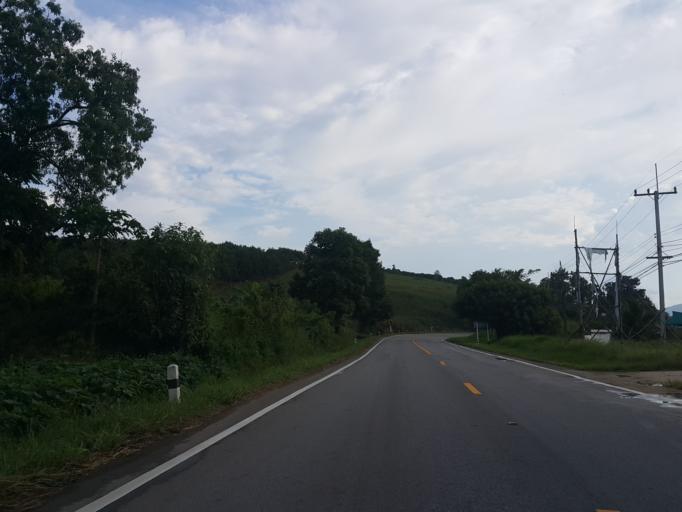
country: TH
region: Chiang Mai
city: Phrao
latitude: 19.2331
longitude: 99.1861
